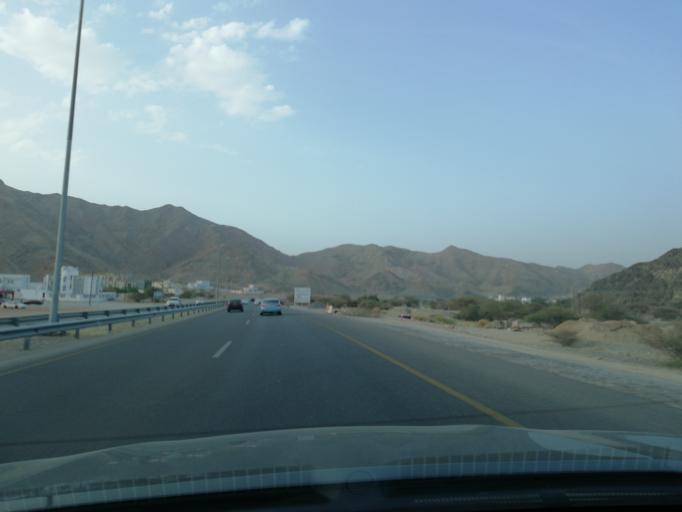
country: OM
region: Muhafazat ad Dakhiliyah
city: Bidbid
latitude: 23.4066
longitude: 58.0803
